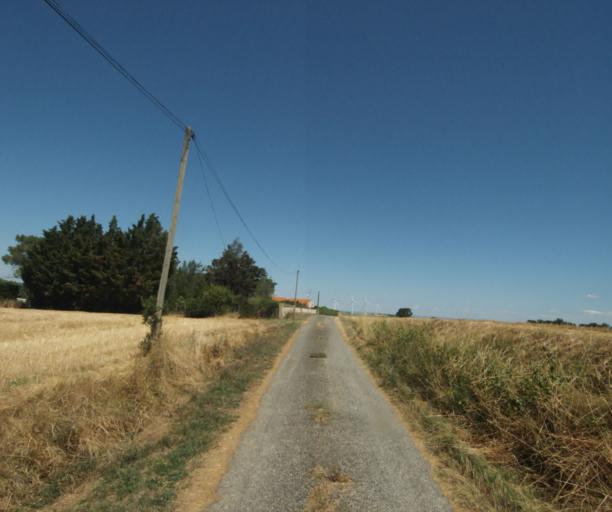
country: FR
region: Midi-Pyrenees
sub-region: Departement de la Haute-Garonne
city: Saint-Felix-Lauragais
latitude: 43.4513
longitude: 1.9002
